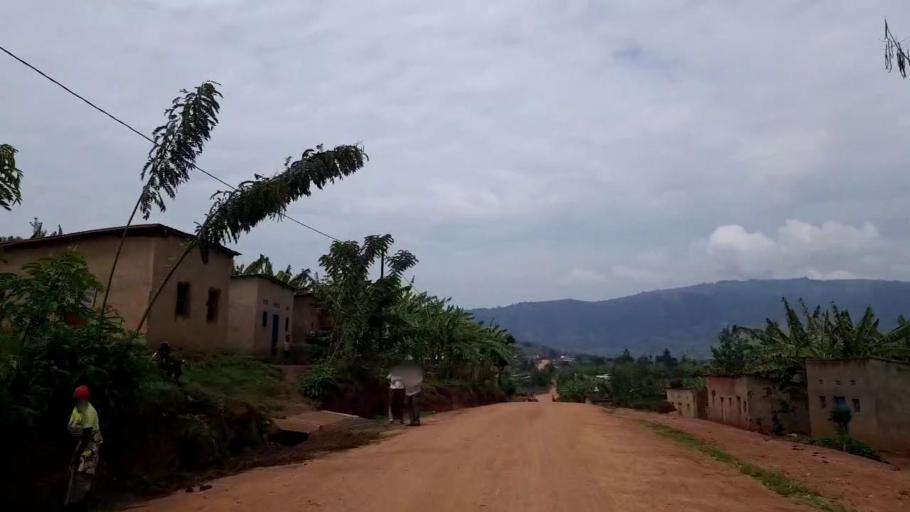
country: RW
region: Northern Province
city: Byumba
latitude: -1.4980
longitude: 30.2226
